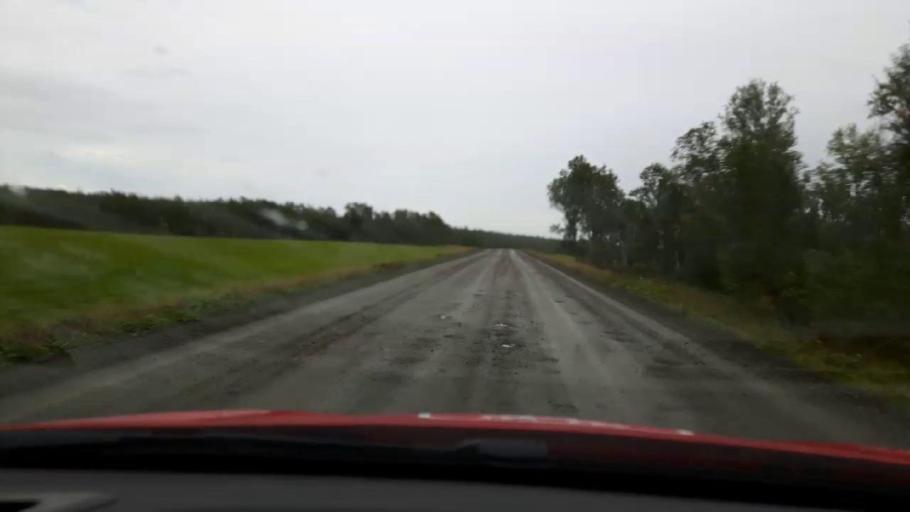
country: NO
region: Nord-Trondelag
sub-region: Meraker
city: Meraker
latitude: 63.5796
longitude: 12.2705
